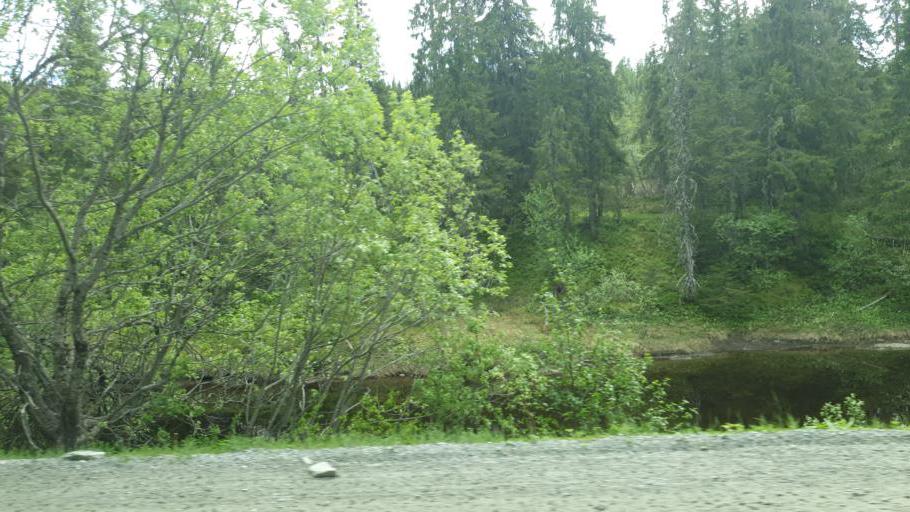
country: NO
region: Sor-Trondelag
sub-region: Trondheim
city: Trondheim
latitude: 63.6780
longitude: 10.3404
